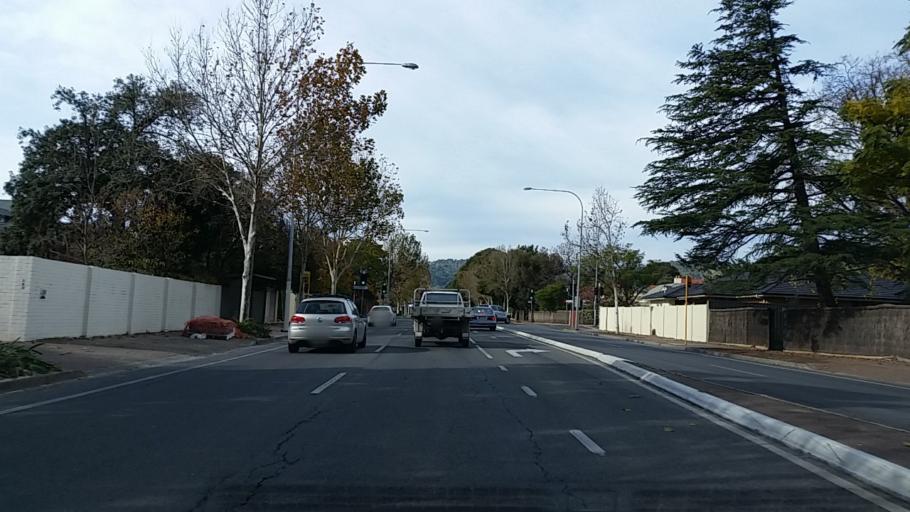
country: AU
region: South Australia
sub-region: Unley
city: Unley Park
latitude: -34.9651
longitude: 138.6144
